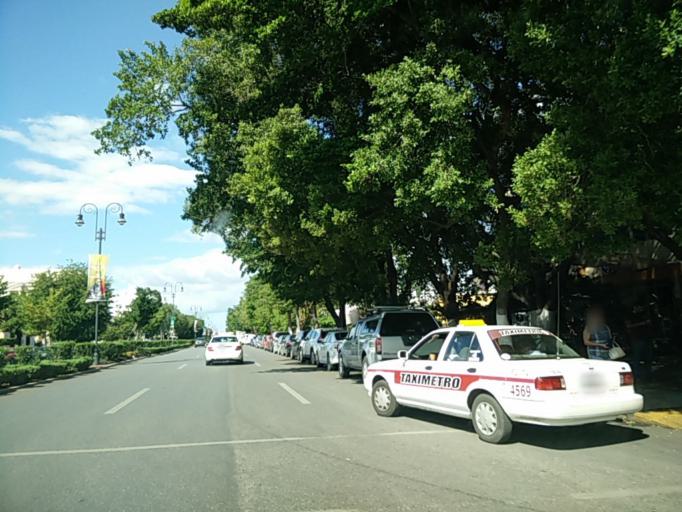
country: MX
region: Yucatan
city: Merida
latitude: 20.9763
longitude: -89.6193
